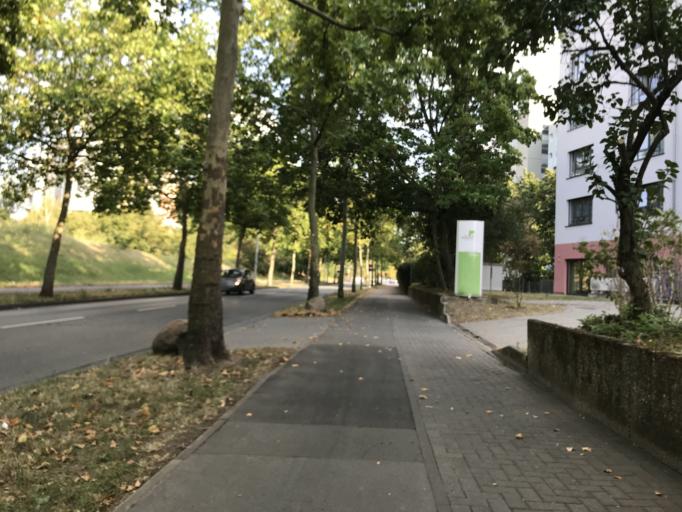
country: DE
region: Rheinland-Pfalz
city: Mainz
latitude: 50.0154
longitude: 8.2951
